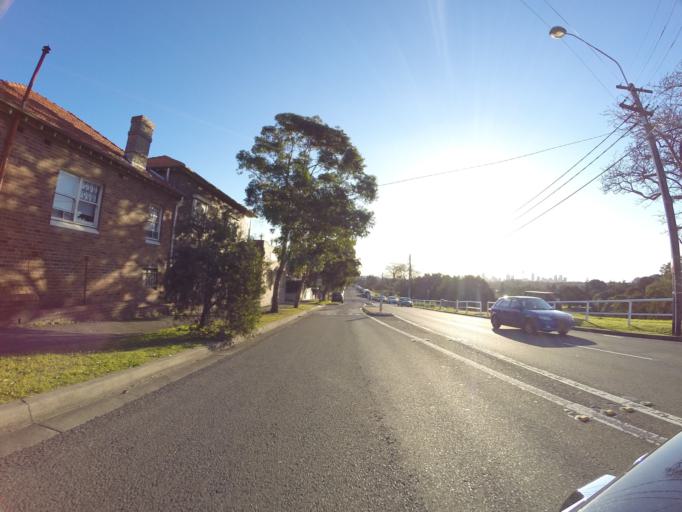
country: AU
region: New South Wales
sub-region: Randwick
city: Clovelly
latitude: -33.9040
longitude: 151.2528
